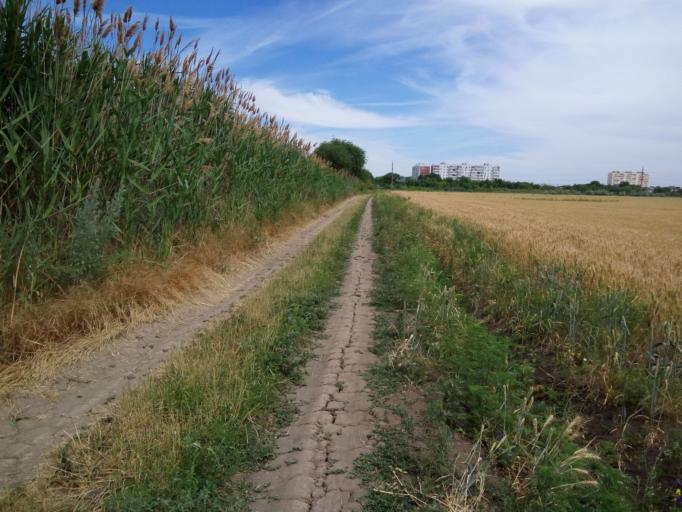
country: RU
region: Rostov
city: Bataysk
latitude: 47.1213
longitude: 39.7252
